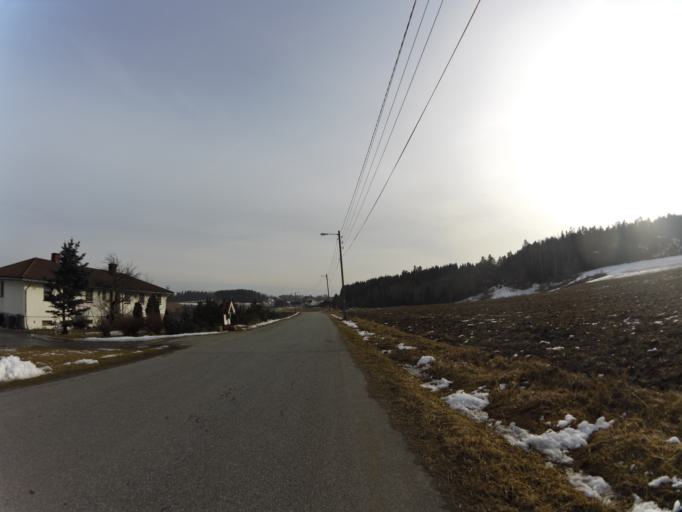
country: NO
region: Ostfold
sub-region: Fredrikstad
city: Fredrikstad
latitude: 59.2773
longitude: 11.0017
